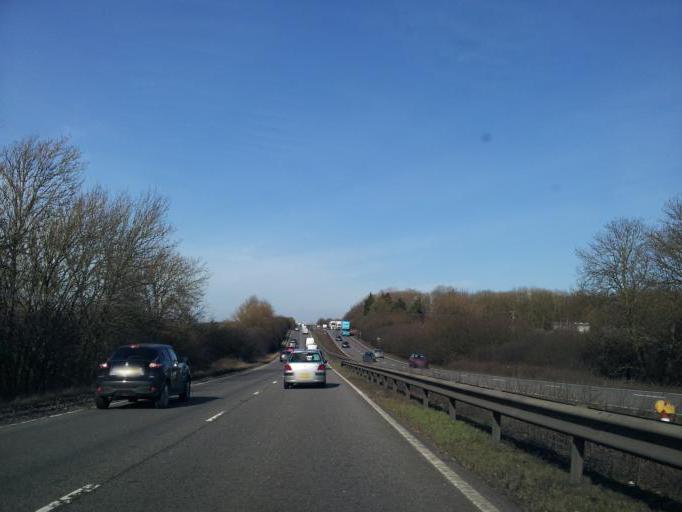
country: GB
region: England
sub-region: District of Rutland
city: Clipsham
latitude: 52.7912
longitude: -0.6107
